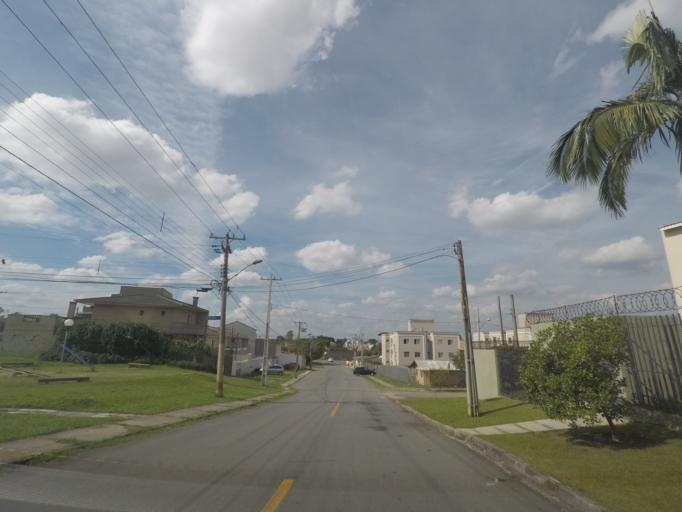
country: BR
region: Parana
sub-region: Sao Jose Dos Pinhais
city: Sao Jose dos Pinhais
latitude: -25.4934
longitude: -49.2557
